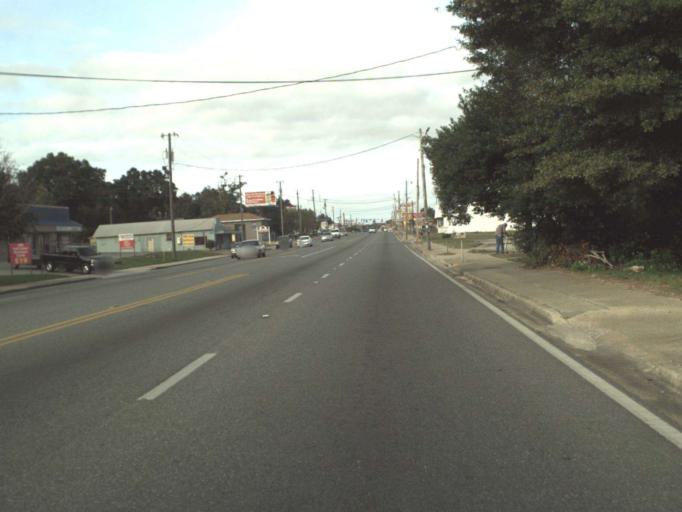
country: US
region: Florida
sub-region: Escambia County
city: Goulding
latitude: 30.4374
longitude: -87.2402
